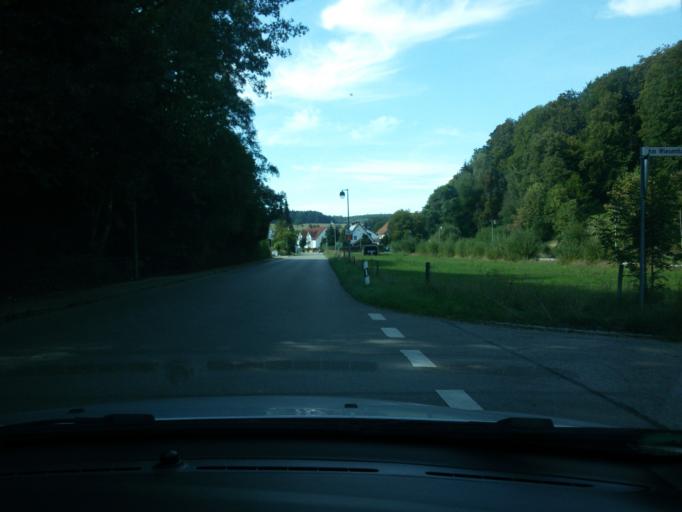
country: DE
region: Bavaria
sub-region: Swabia
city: Mickhausen
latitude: 48.2426
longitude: 10.6434
